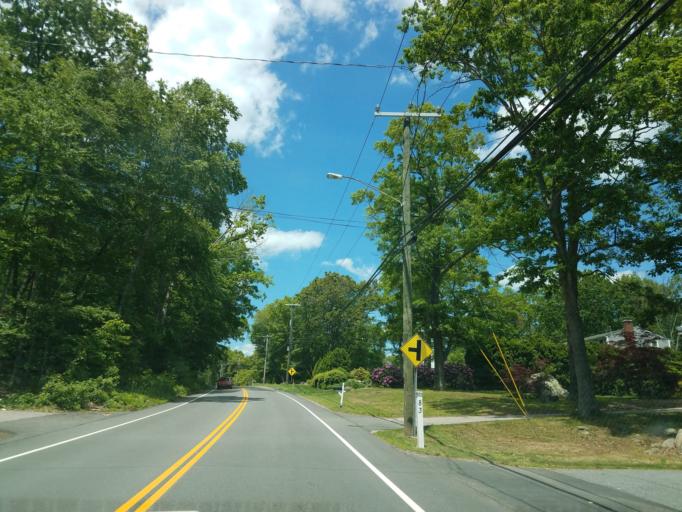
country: US
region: Connecticut
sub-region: New London County
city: Niantic
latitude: 41.3749
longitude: -72.2122
